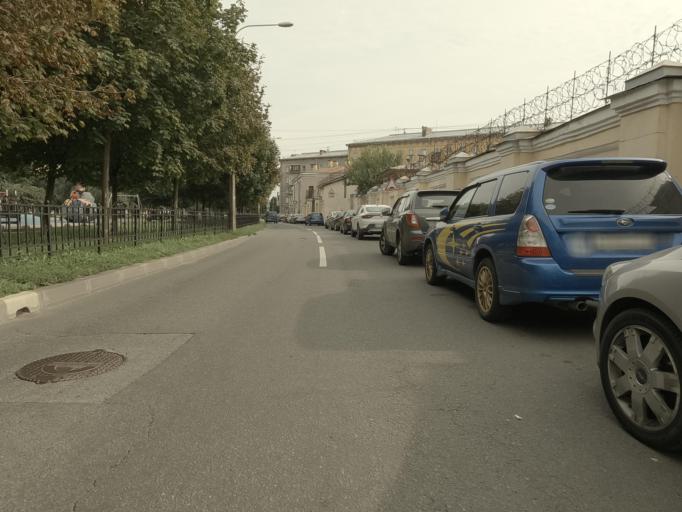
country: RU
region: St.-Petersburg
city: Admiralteisky
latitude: 59.9127
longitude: 30.2841
